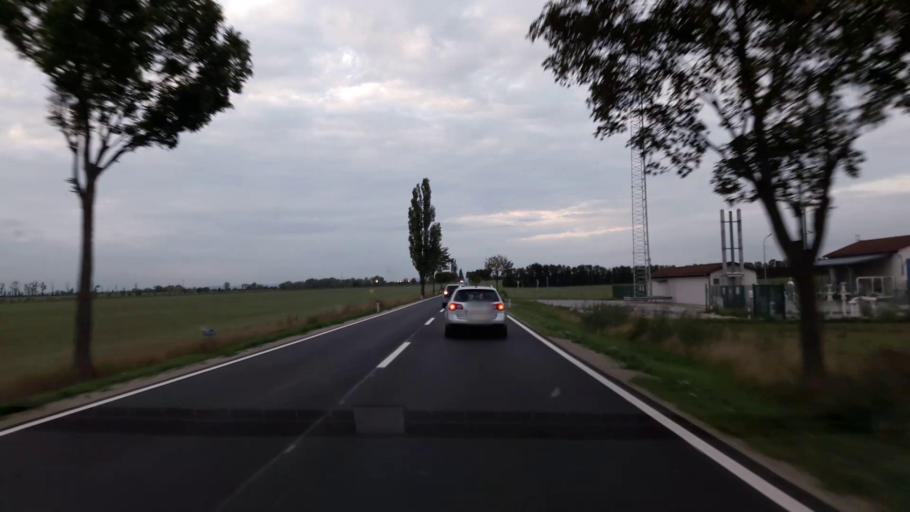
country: AT
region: Lower Austria
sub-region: Politischer Bezirk Wien-Umgebung
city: Rauchenwarth
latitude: 48.1225
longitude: 16.5097
